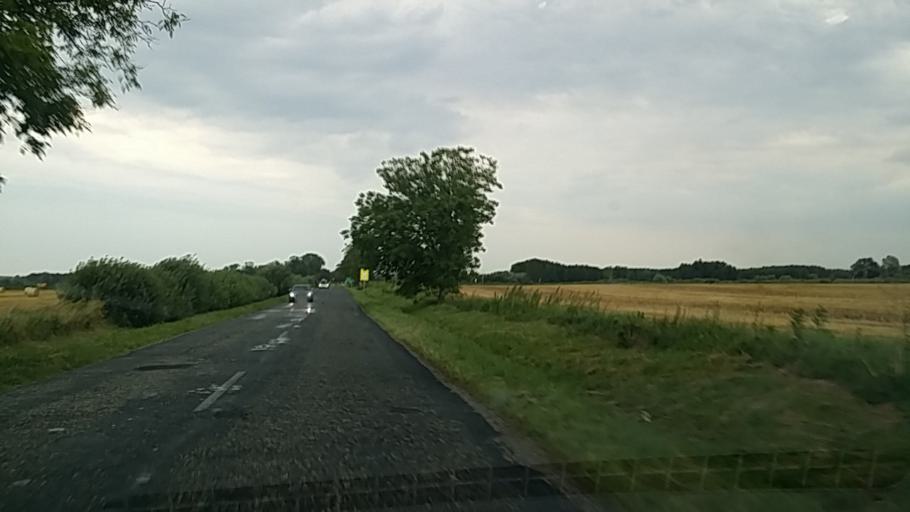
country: HU
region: Zala
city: Zalakomar
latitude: 46.5217
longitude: 17.1413
